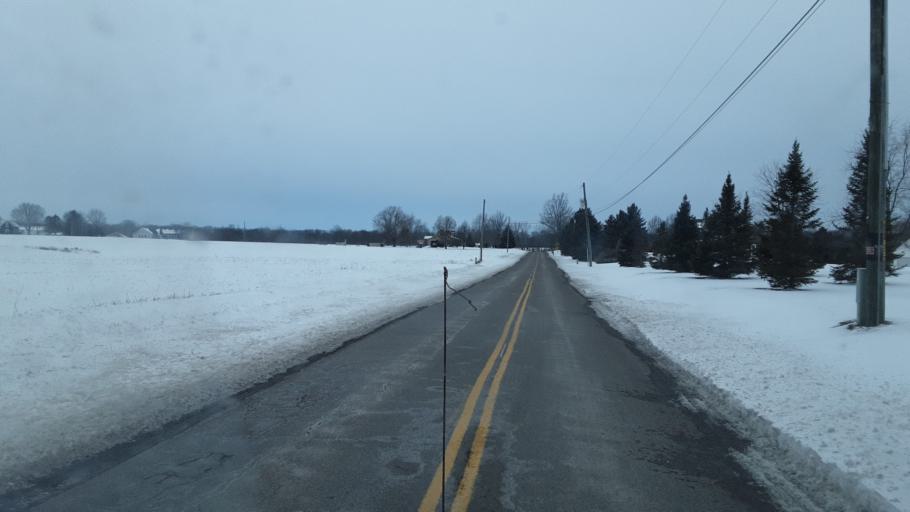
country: US
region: Ohio
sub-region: Madison County
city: Plain City
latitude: 40.1355
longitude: -83.2815
